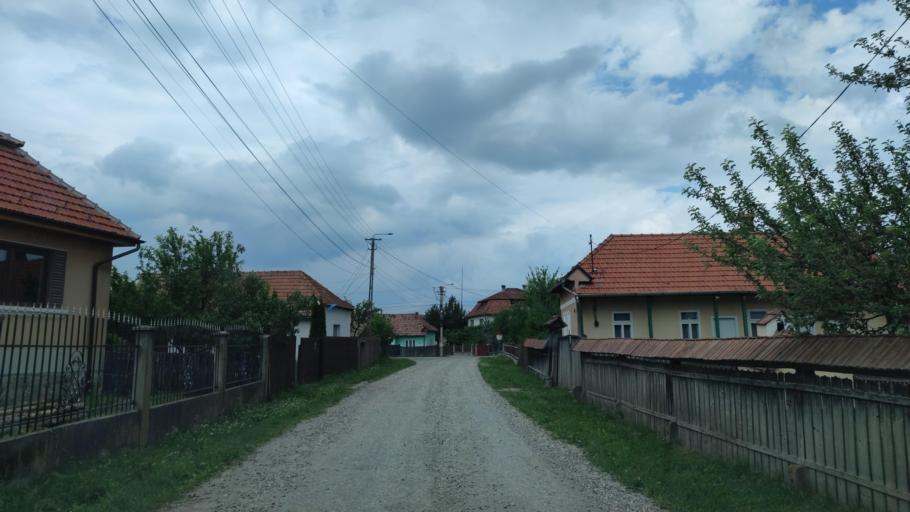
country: RO
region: Harghita
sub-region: Comuna Remetea
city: Remetea
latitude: 46.8037
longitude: 25.4552
